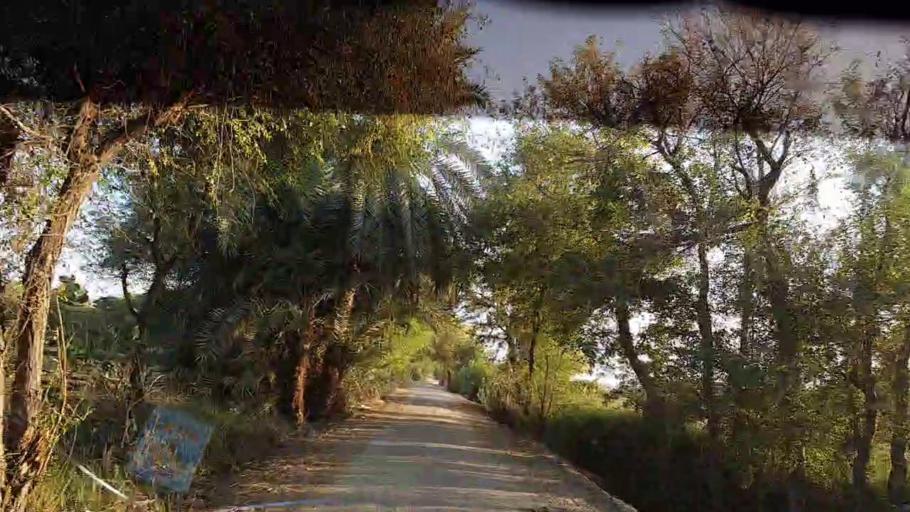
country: PK
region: Sindh
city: Ratodero
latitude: 27.8705
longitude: 68.1879
